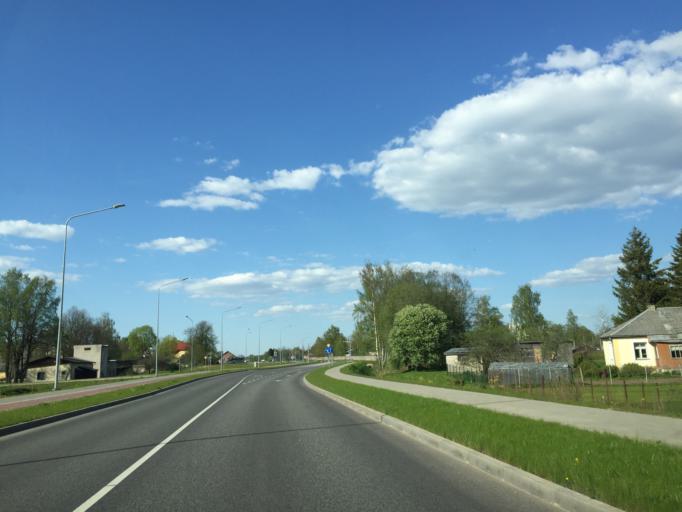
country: LV
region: Limbazu Rajons
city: Limbazi
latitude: 57.5061
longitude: 24.7214
